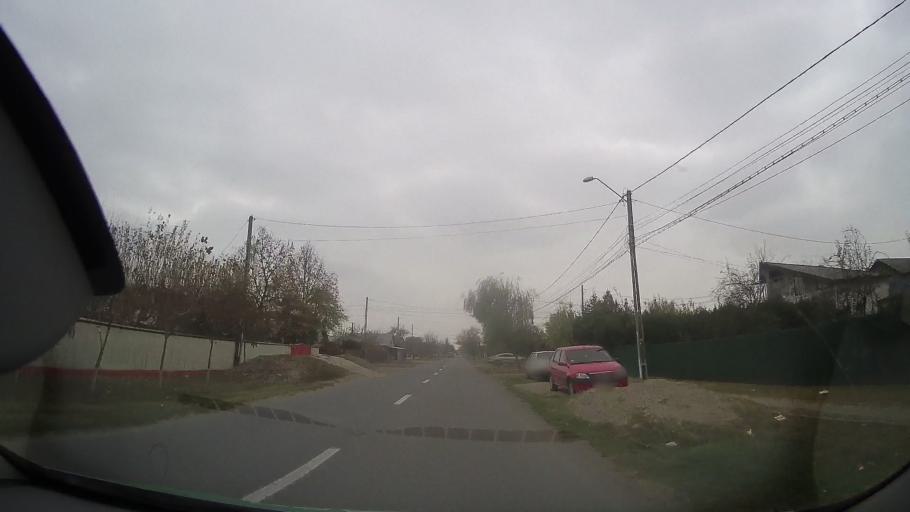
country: RO
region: Ialomita
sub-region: Comuna Manasia
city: Manasia
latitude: 44.7137
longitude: 26.6785
